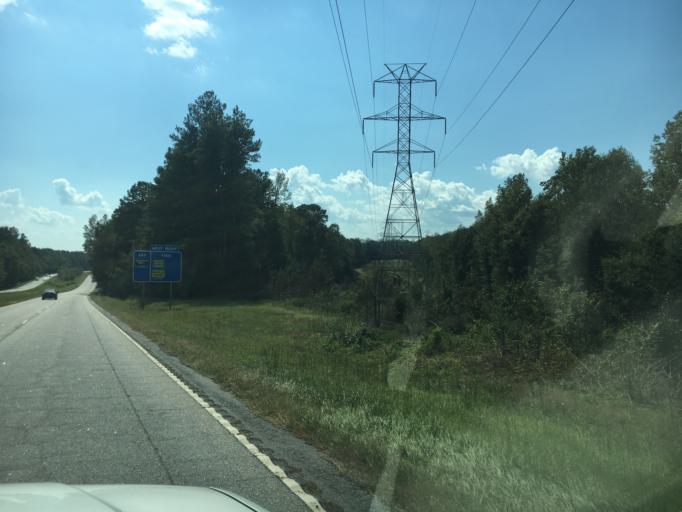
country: US
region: South Carolina
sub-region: Pickens County
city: Central
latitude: 34.7159
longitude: -82.7475
